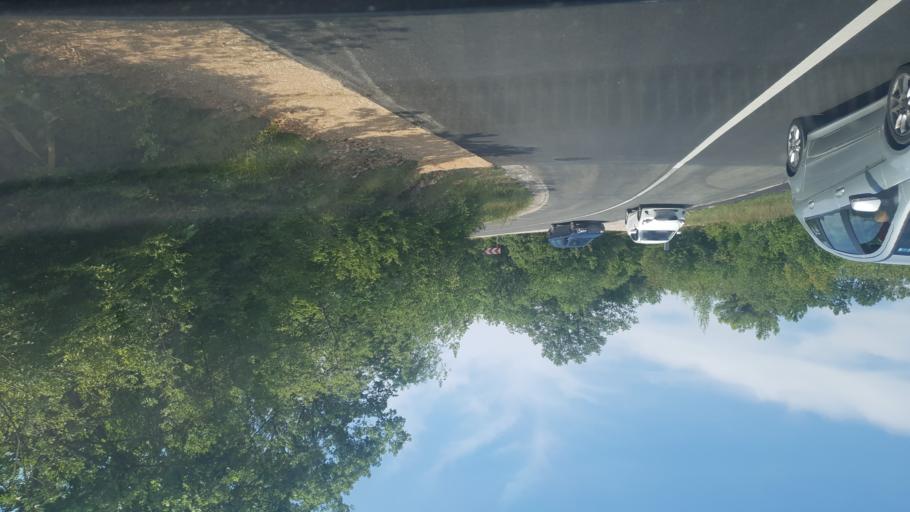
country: HR
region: Primorsko-Goranska
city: Njivice
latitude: 45.1467
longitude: 14.6093
